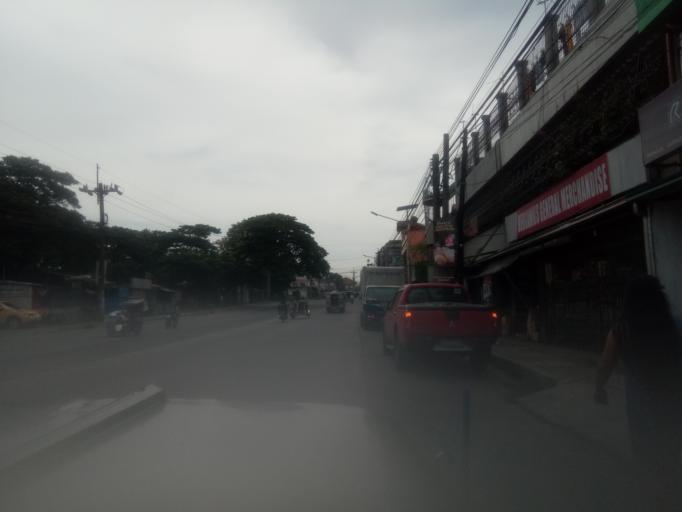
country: PH
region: Calabarzon
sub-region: Province of Cavite
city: Bulihan
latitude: 14.2916
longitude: 121.0048
